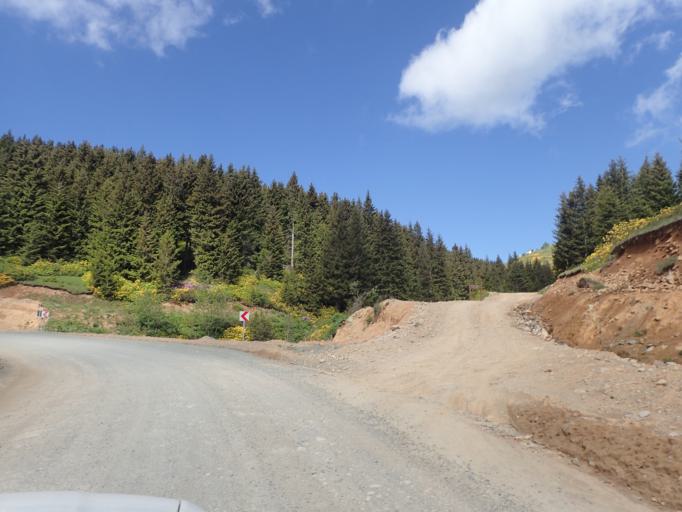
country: TR
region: Ordu
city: Topcam
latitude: 40.6502
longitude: 37.9379
